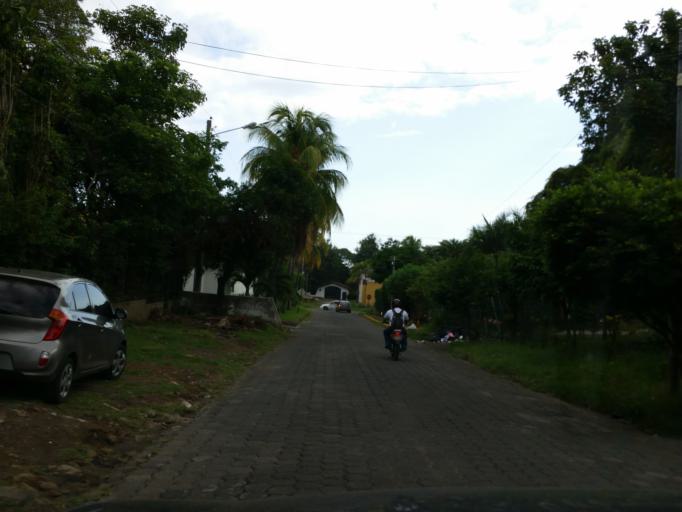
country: NI
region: Managua
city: Managua
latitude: 12.0988
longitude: -86.2356
